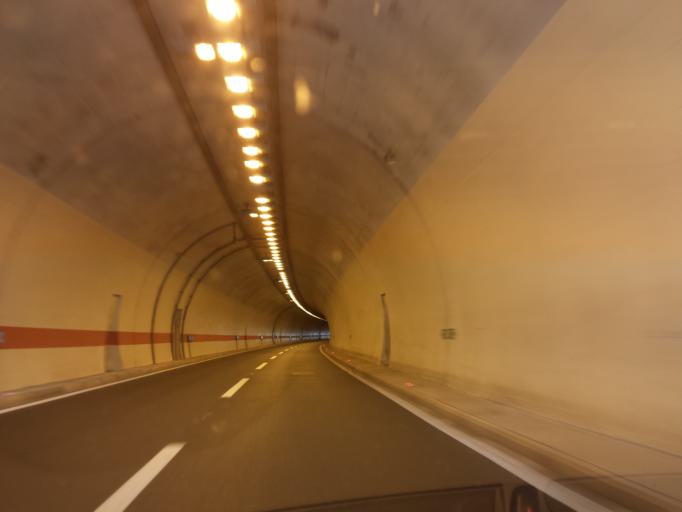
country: HR
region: Splitsko-Dalmatinska
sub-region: Grad Omis
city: Omis
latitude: 43.4832
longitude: 16.8031
